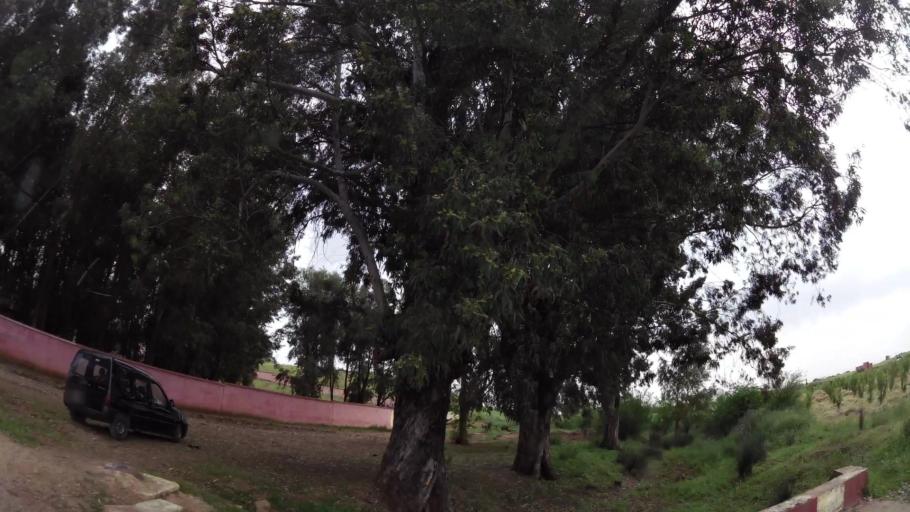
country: MA
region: Rabat-Sale-Zemmour-Zaer
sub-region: Khemisset
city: Khemisset
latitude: 33.7456
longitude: -6.1990
